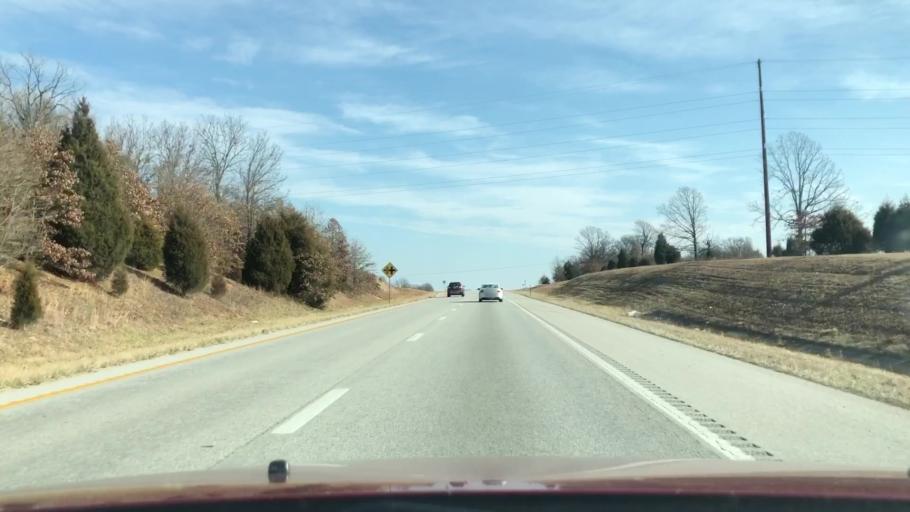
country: US
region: Missouri
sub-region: Webster County
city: Rogersville
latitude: 37.1208
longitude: -93.0048
